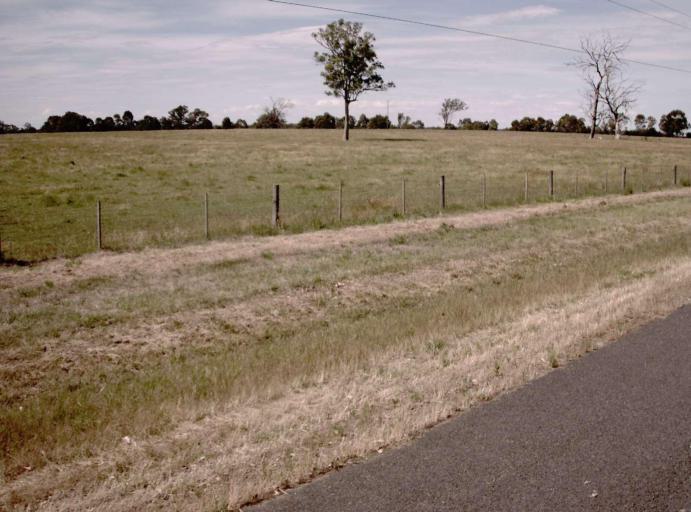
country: AU
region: Victoria
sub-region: Wellington
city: Sale
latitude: -37.9212
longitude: 147.2511
